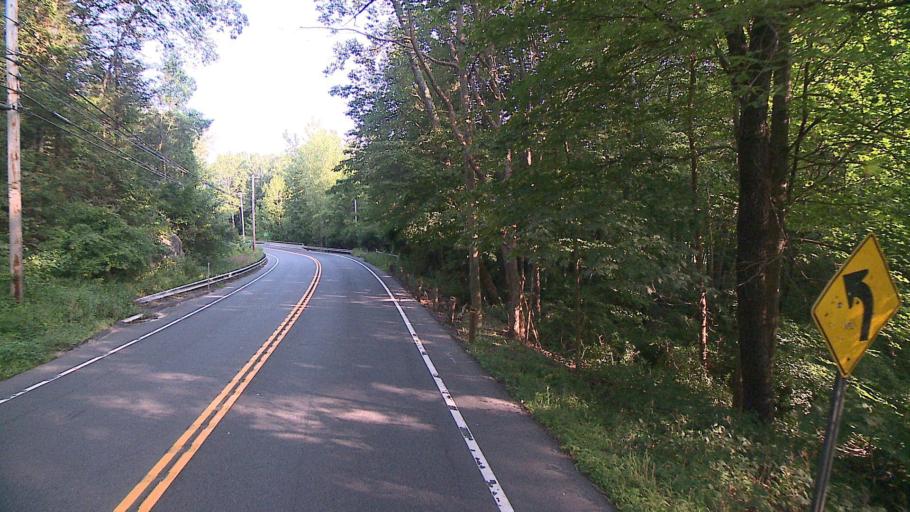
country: US
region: Connecticut
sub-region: Fairfield County
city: Sherman
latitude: 41.6363
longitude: -73.4768
